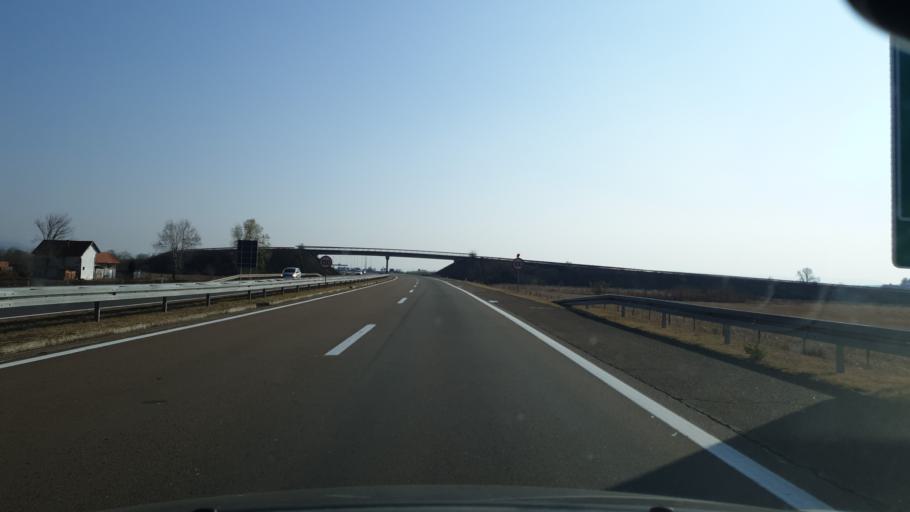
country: RS
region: Central Serbia
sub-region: Nisavski Okrug
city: Doljevac
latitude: 43.2064
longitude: 21.8389
